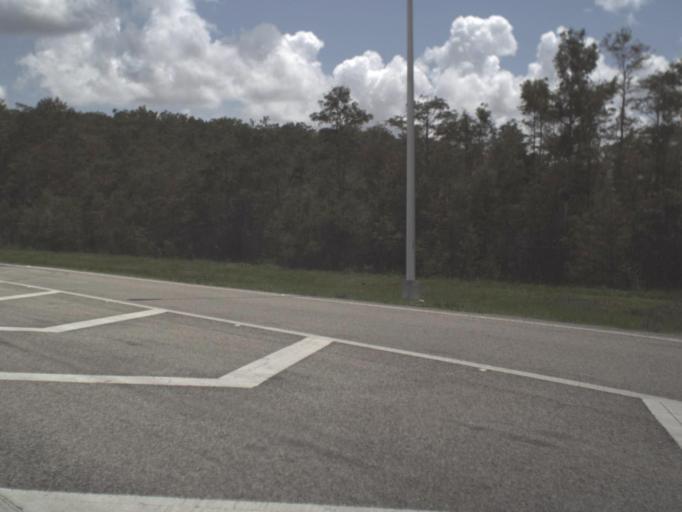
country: US
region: Florida
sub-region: Collier County
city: Immokalee
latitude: 26.1682
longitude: -81.0845
